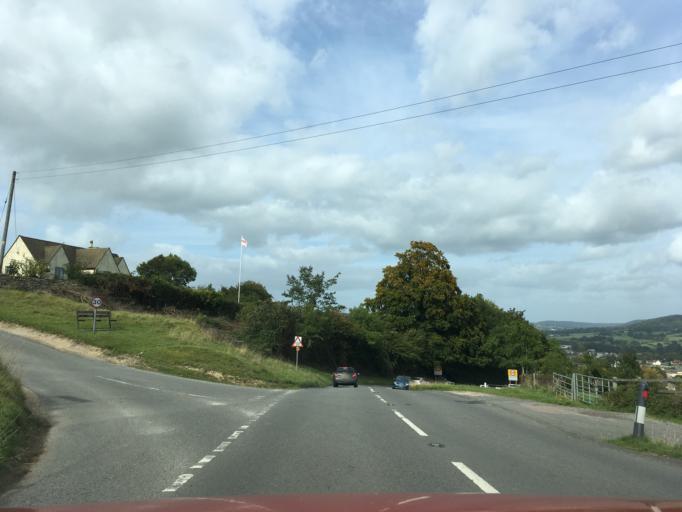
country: GB
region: England
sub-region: Gloucestershire
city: Nailsworth
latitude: 51.7308
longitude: -2.2429
